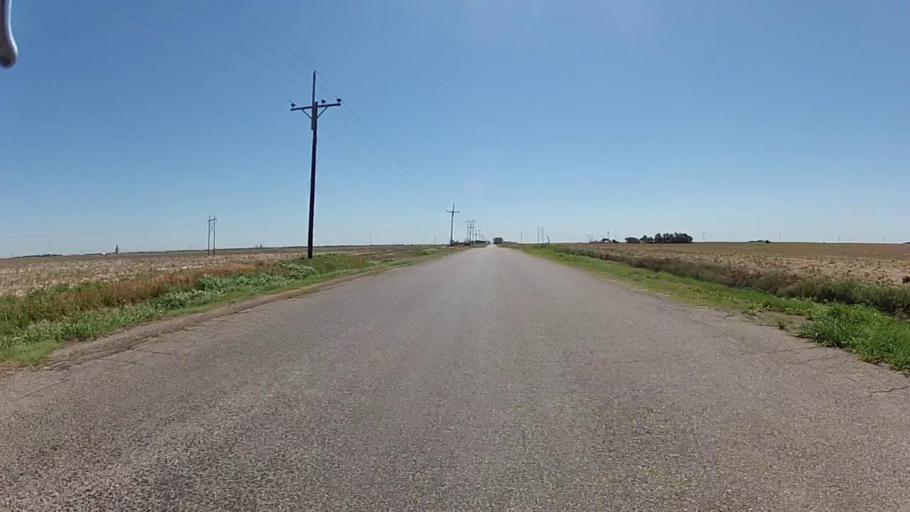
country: US
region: Kansas
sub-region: Kiowa County
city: Greensburg
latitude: 37.5867
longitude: -99.3440
